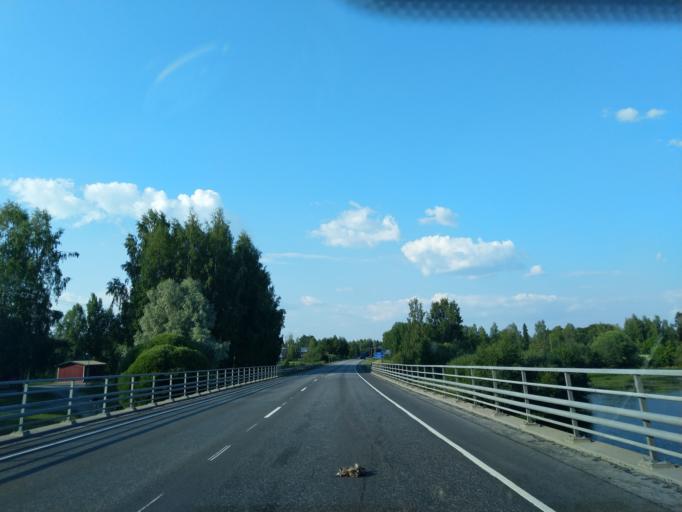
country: FI
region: Satakunta
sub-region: Pori
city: Pomarkku
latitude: 61.6959
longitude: 22.0054
